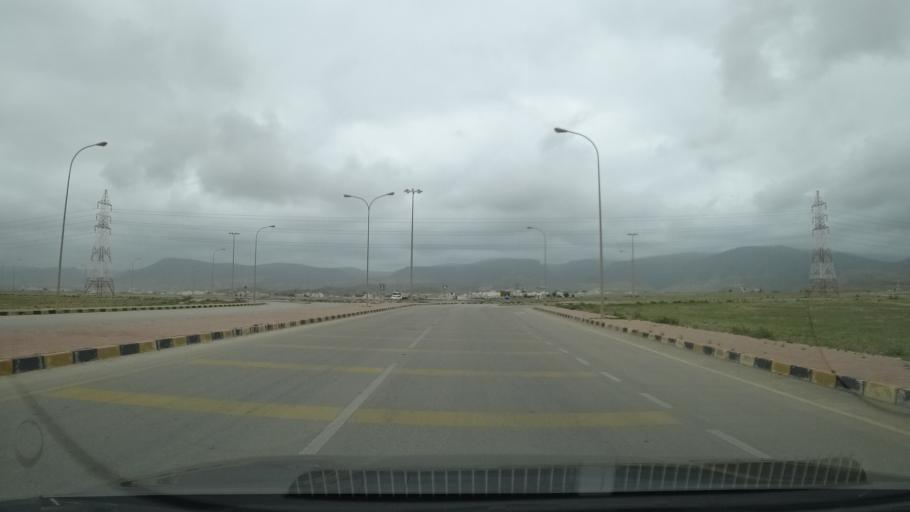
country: OM
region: Zufar
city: Salalah
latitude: 17.1021
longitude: 54.2168
